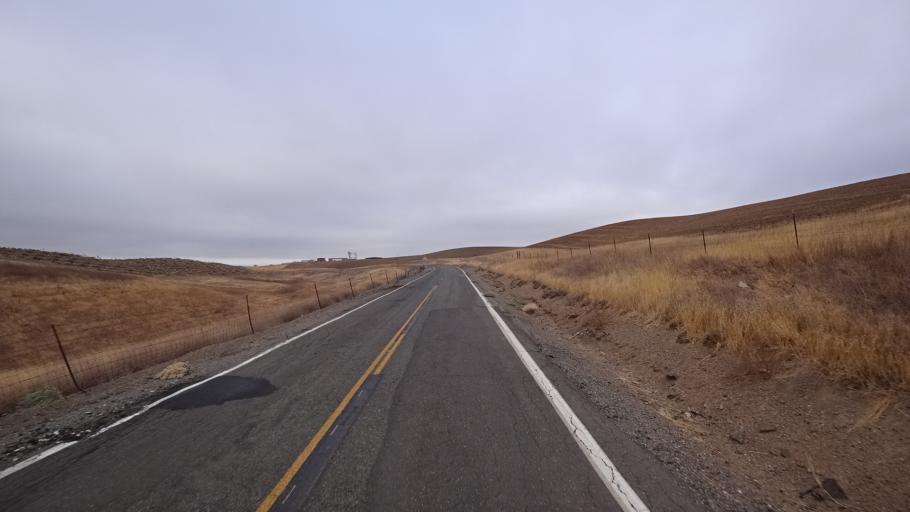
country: US
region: California
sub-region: Yolo County
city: Dunnigan
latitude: 38.8857
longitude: -122.0144
